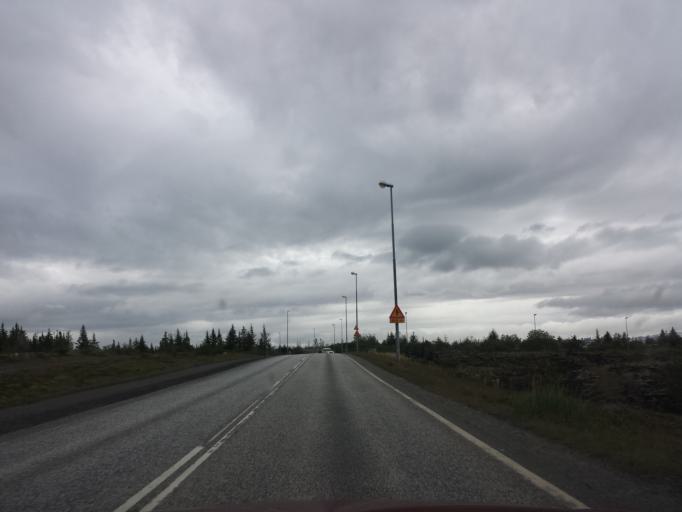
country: IS
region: Capital Region
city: Hafnarfjoerdur
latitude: 64.0855
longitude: -21.9709
